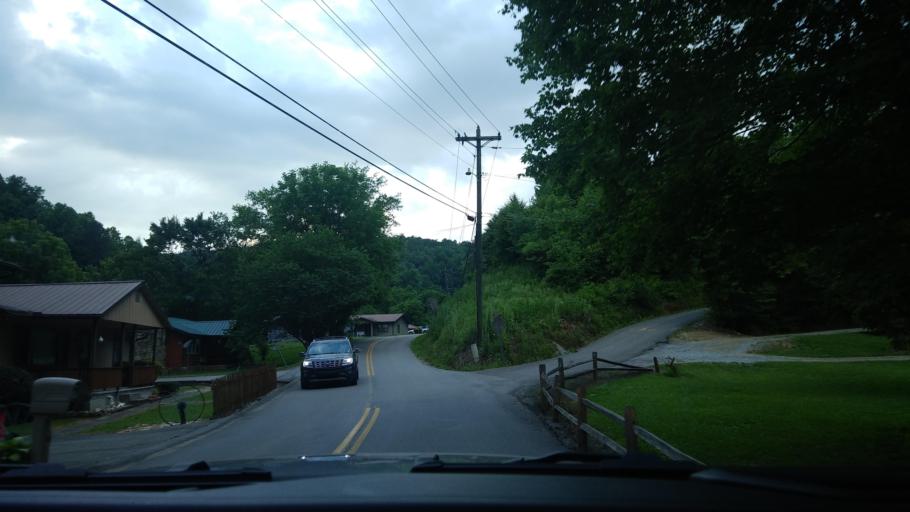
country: US
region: Tennessee
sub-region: Sevier County
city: Gatlinburg
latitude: 35.7349
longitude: -83.4838
